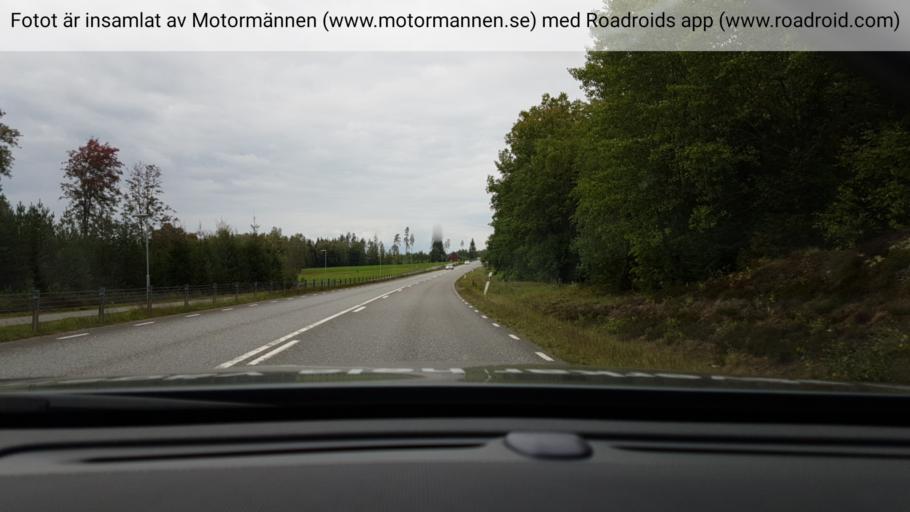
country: SE
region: Joenkoeping
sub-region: Gislaveds Kommun
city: Smalandsstenar
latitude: 57.1316
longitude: 13.3801
